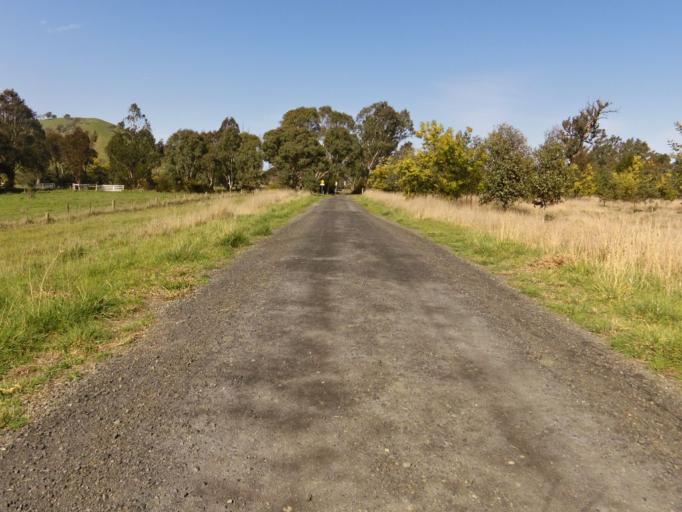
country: AU
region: Victoria
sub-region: Murrindindi
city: Alexandra
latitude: -37.0176
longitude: 145.7986
